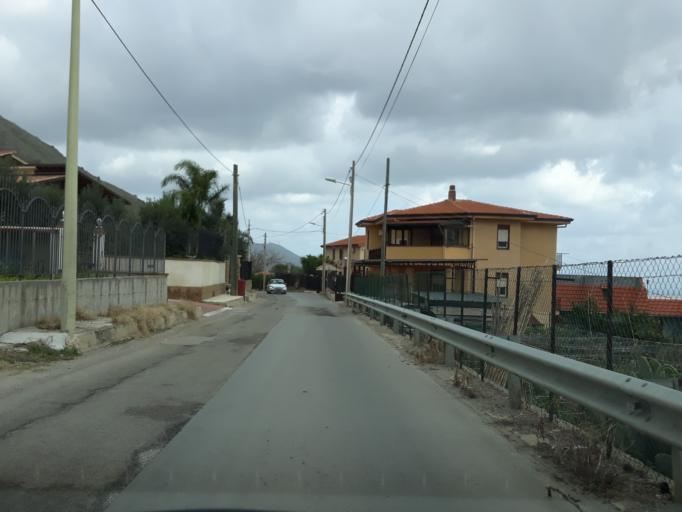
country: IT
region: Sicily
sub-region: Palermo
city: Monreale
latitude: 38.0820
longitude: 13.2973
